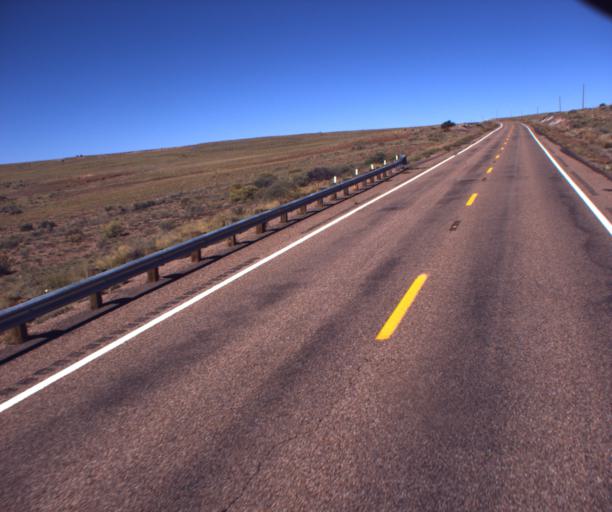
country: US
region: Arizona
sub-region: Apache County
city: Saint Johns
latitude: 34.5260
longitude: -109.4564
